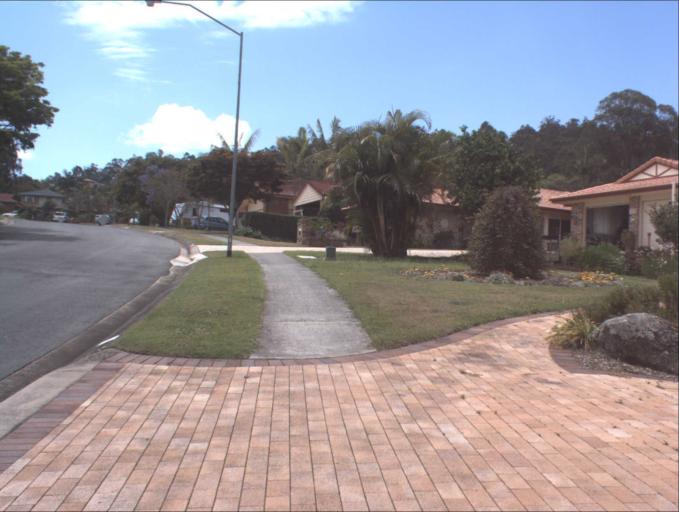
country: AU
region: Queensland
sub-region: Logan
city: Slacks Creek
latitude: -27.6423
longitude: 153.1810
